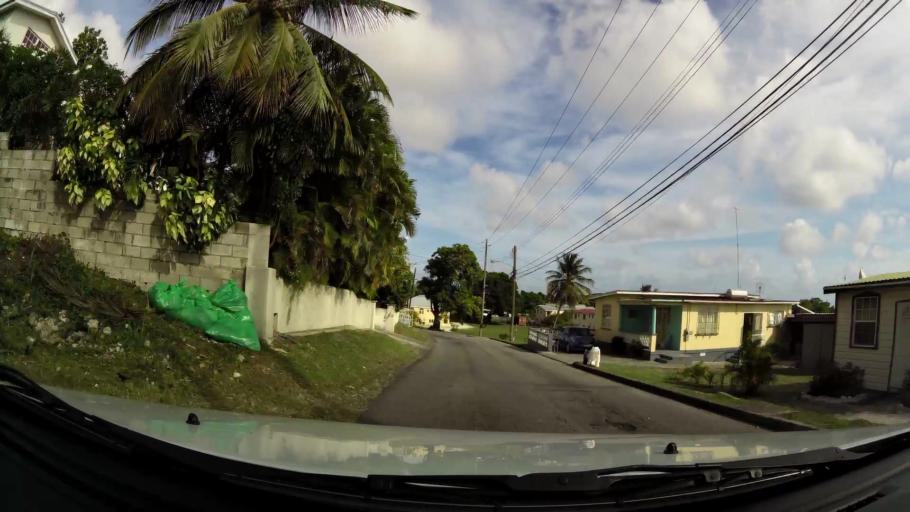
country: BB
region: Saint Michael
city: Bridgetown
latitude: 13.0863
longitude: -59.5845
